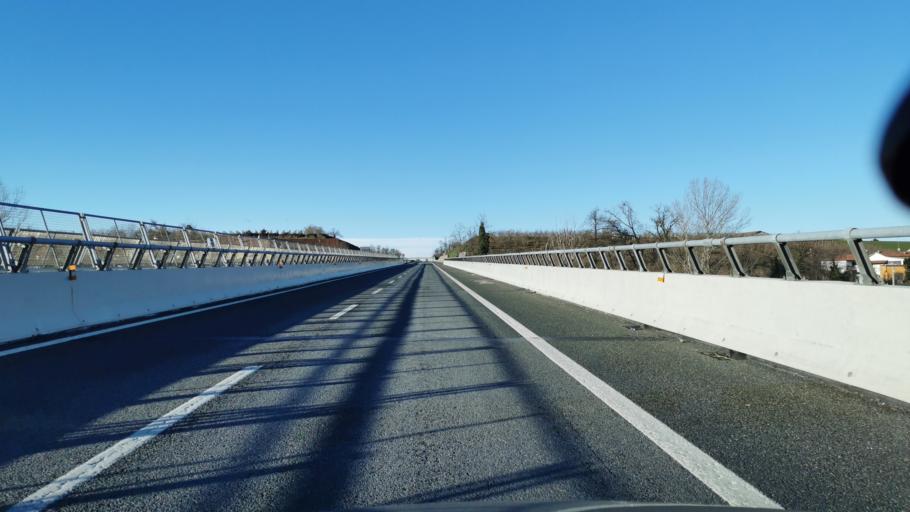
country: IT
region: Piedmont
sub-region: Provincia di Cuneo
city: Magliano Alpi
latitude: 44.4673
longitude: 7.8314
